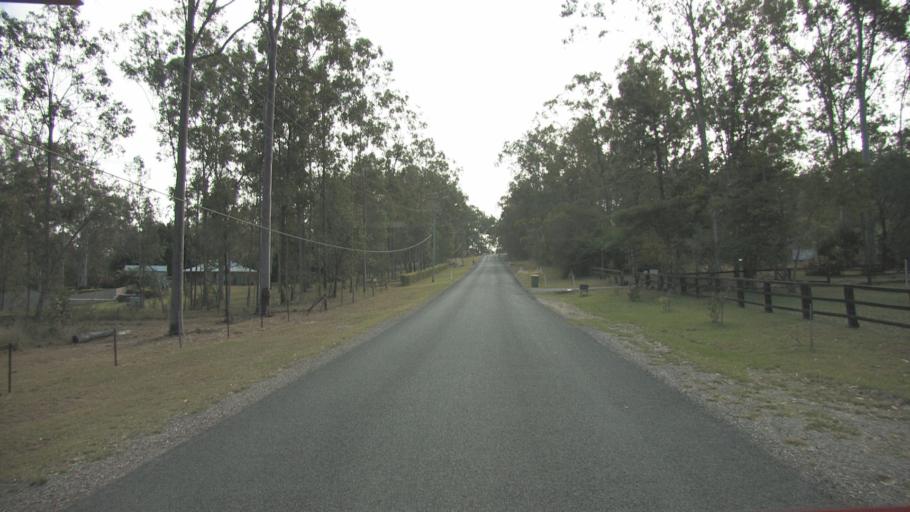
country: AU
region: Queensland
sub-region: Logan
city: North Maclean
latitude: -27.7733
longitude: 152.9654
